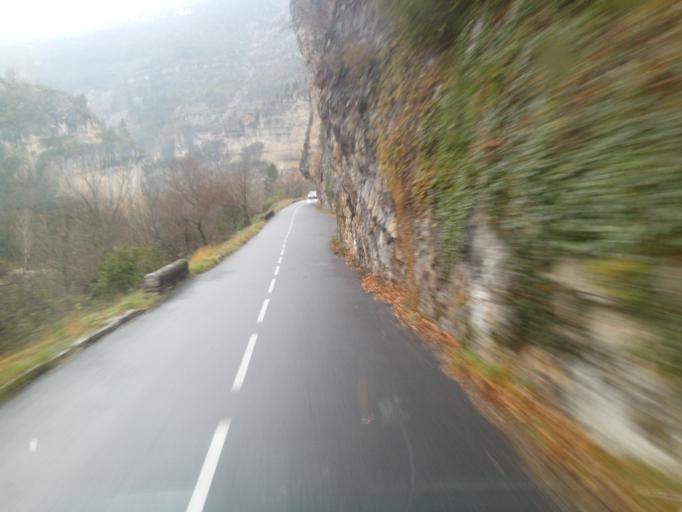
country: FR
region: Languedoc-Roussillon
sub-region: Departement de la Lozere
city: Chanac
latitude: 44.3411
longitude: 3.3858
